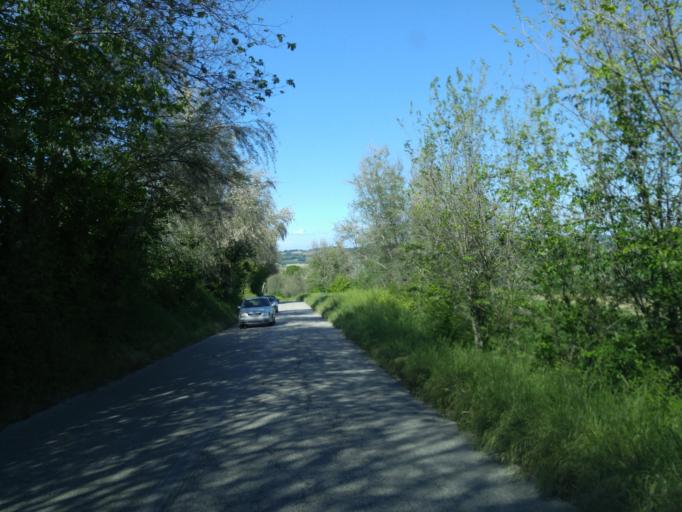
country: IT
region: The Marches
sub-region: Provincia di Pesaro e Urbino
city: Mombaroccio
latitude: 43.8234
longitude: 12.8519
